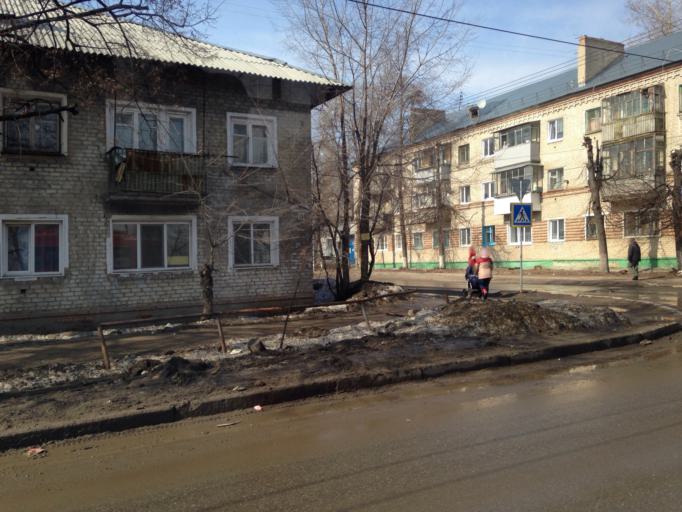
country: RU
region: Ulyanovsk
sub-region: Ulyanovskiy Rayon
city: Ulyanovsk
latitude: 54.3480
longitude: 48.5483
